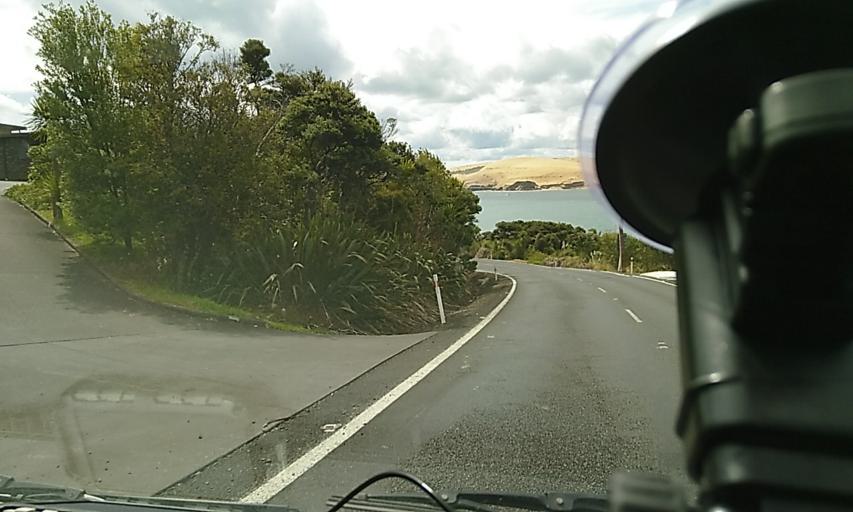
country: NZ
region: Northland
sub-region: Far North District
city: Ahipara
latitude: -35.5387
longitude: 173.3856
